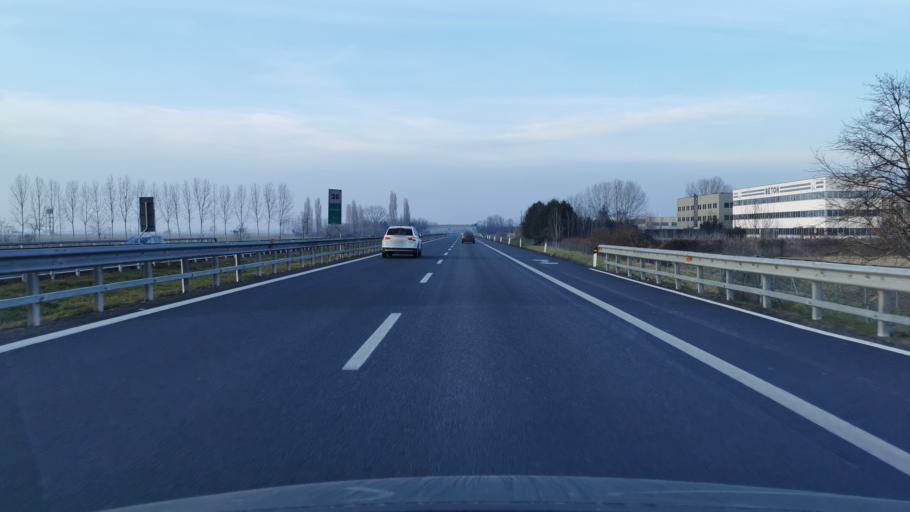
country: IT
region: Piedmont
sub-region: Provincia di Cuneo
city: Sommariva del Bosco
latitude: 44.7373
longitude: 7.7537
